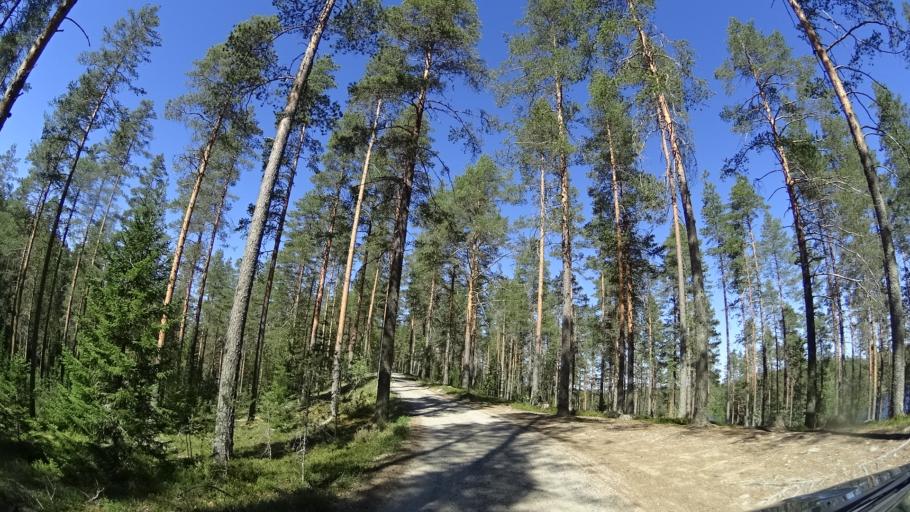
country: FI
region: Kainuu
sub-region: Kajaani
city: Vuolijoki
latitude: 63.9715
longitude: 26.8029
